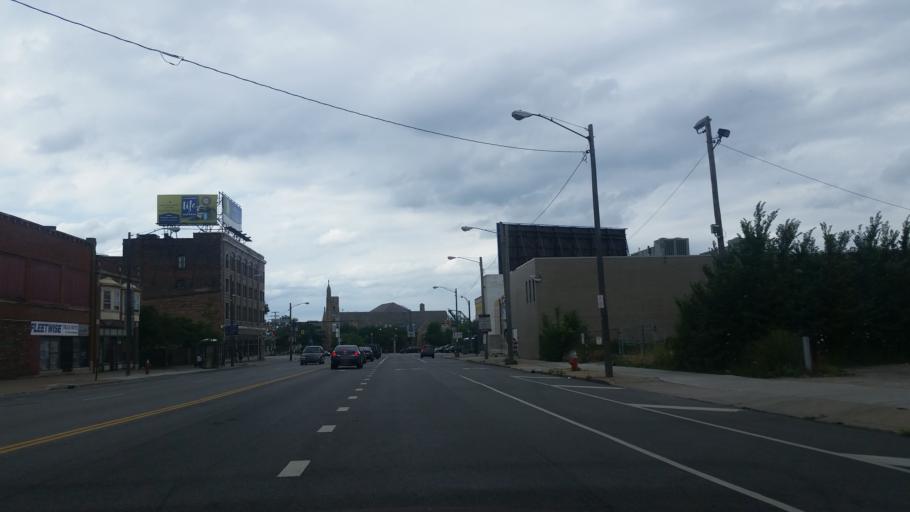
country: US
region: Ohio
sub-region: Cuyahoga County
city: Cleveland
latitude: 41.4902
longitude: -81.7069
